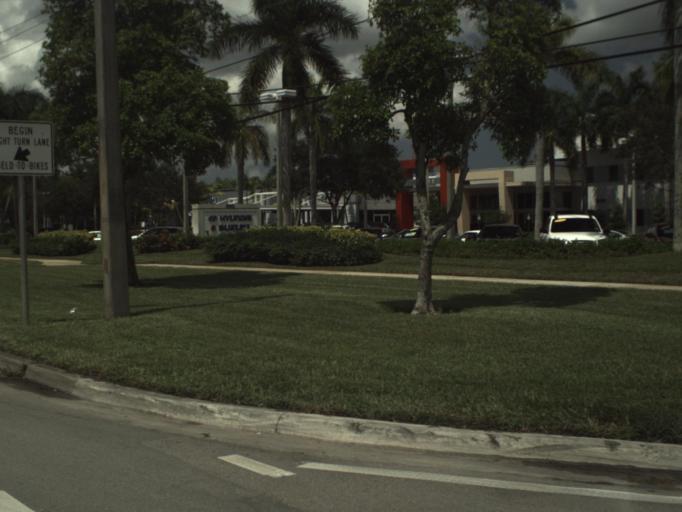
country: US
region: Florida
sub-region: Broward County
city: Parkland
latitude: 26.2917
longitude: -80.2019
